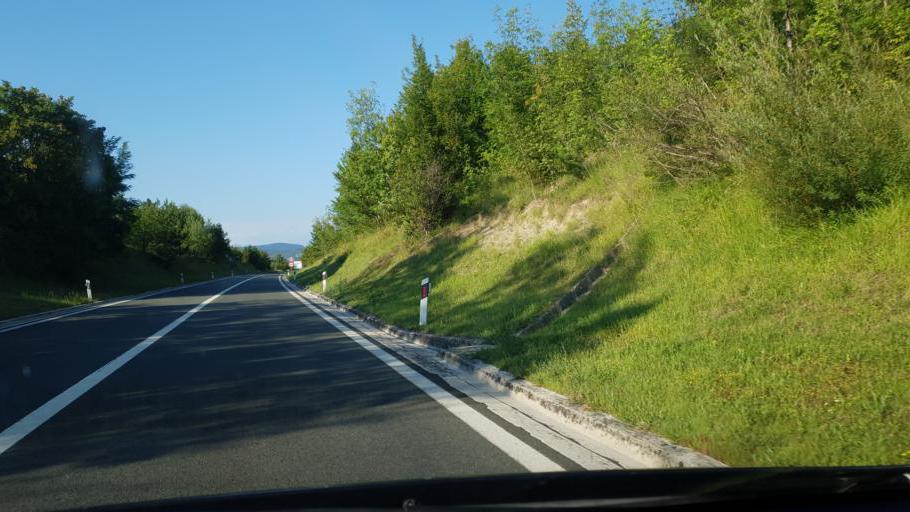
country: HR
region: Istarska
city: Buzet
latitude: 45.3150
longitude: 14.0688
